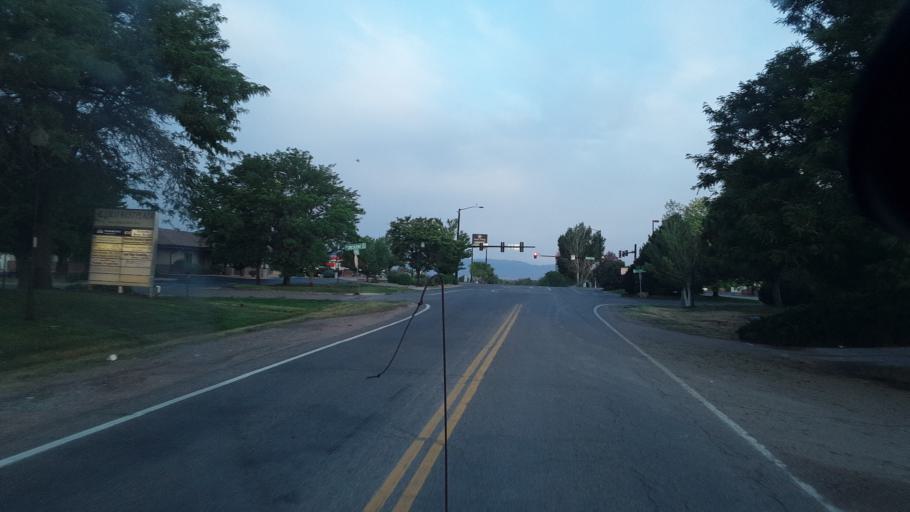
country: US
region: Colorado
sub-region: Pueblo County
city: Pueblo West
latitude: 38.3325
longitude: -104.7428
